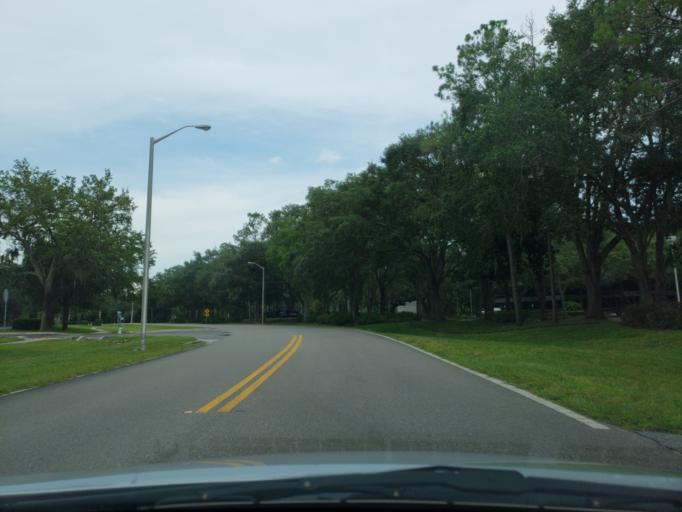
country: US
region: Florida
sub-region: Hillsborough County
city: Temple Terrace
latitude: 28.0600
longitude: -82.3787
